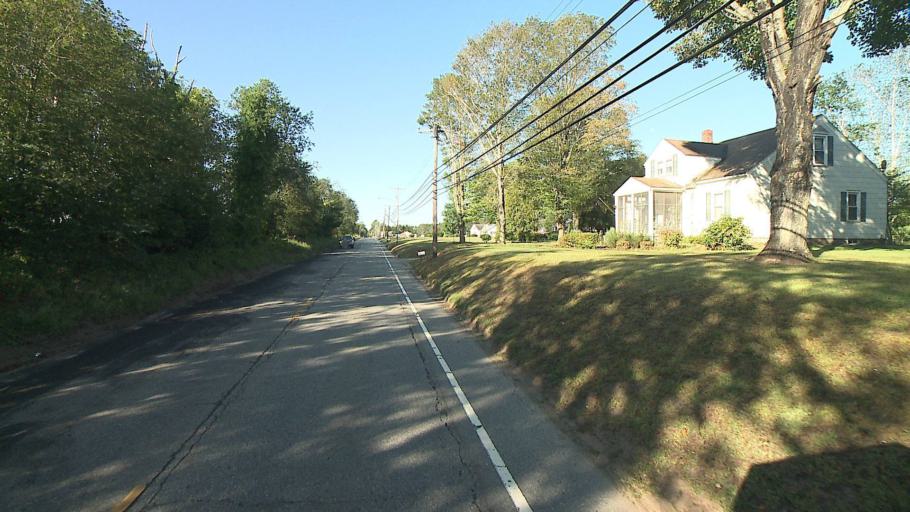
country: US
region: Connecticut
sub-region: Windham County
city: Plainfield Village
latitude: 41.6430
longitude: -71.9435
